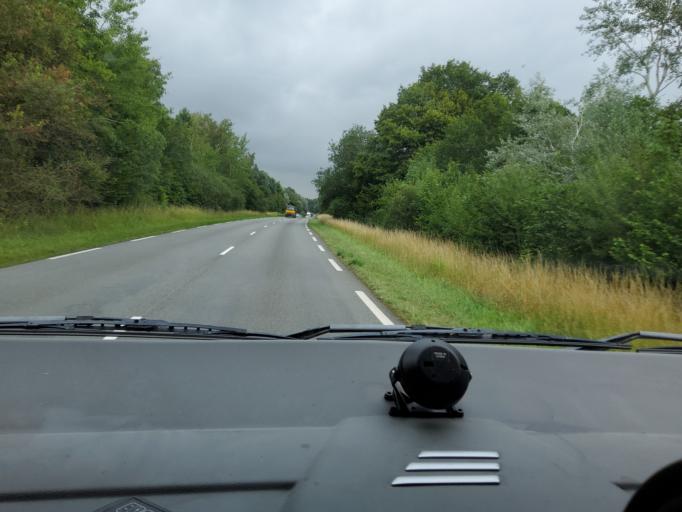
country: FR
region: Nord-Pas-de-Calais
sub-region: Departement du Nord
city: Watten
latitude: 50.8337
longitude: 2.1993
